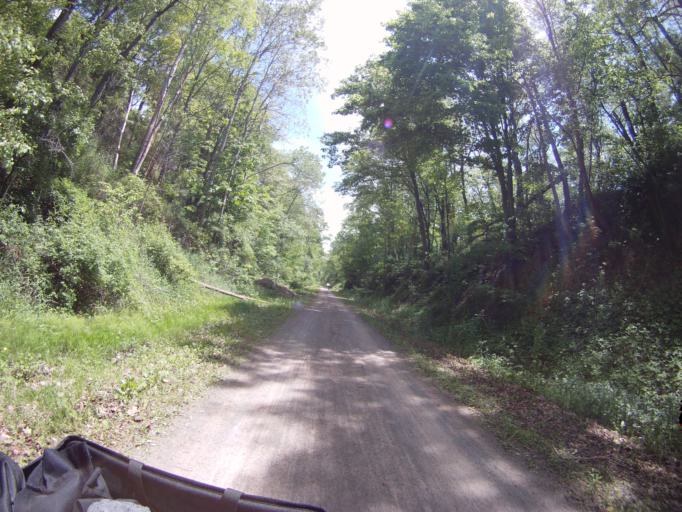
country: US
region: Pennsylvania
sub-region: Somerset County
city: Meyersdale
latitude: 39.8306
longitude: -79.0391
